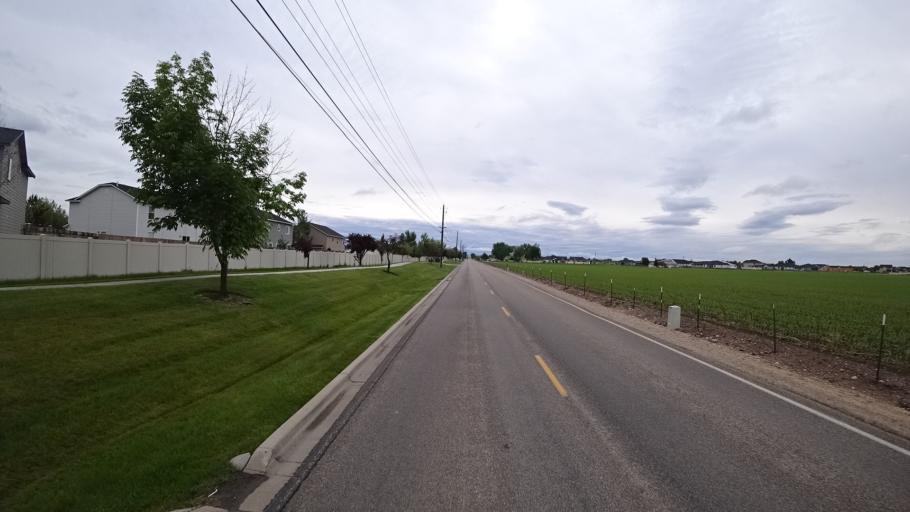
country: US
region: Idaho
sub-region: Ada County
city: Star
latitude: 43.7066
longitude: -116.4865
